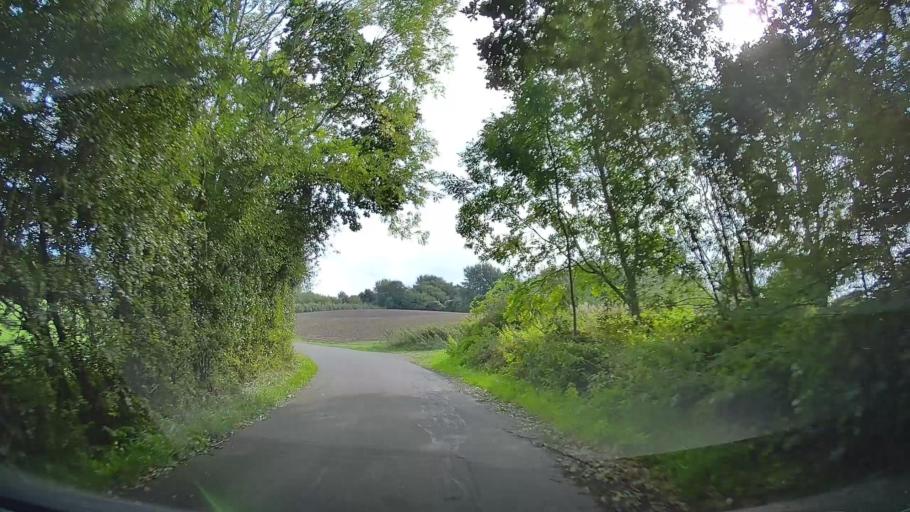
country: DE
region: Schleswig-Holstein
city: Ringsberg
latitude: 54.8285
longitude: 9.6036
